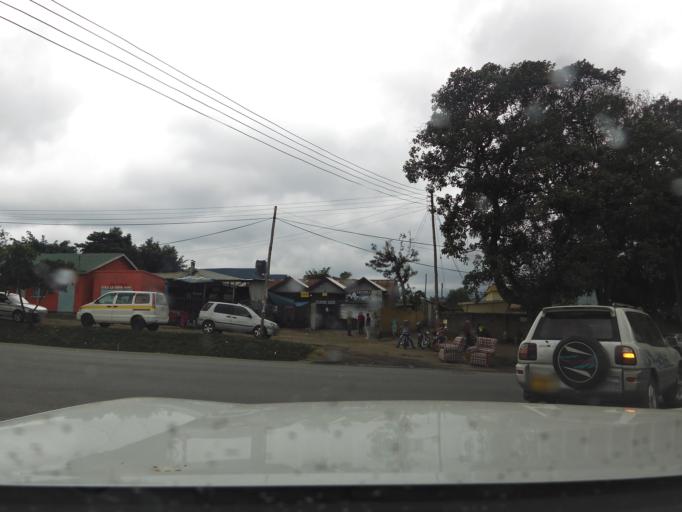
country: TZ
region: Arusha
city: Arusha
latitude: -3.3614
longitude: 36.6904
